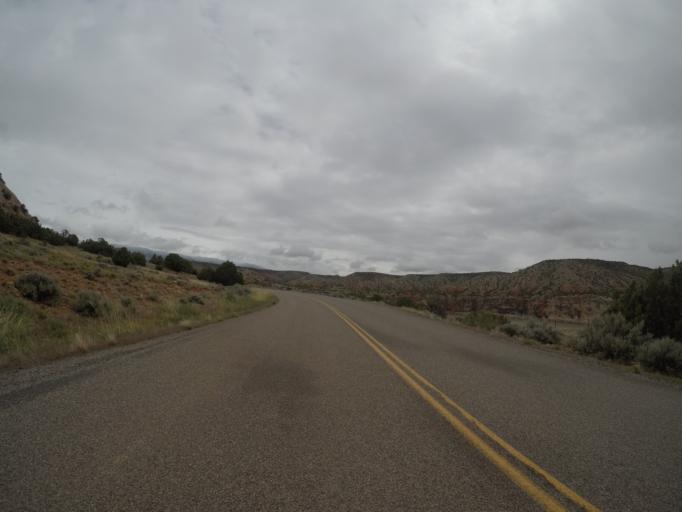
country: US
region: Wyoming
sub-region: Big Horn County
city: Lovell
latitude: 45.0967
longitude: -108.2127
